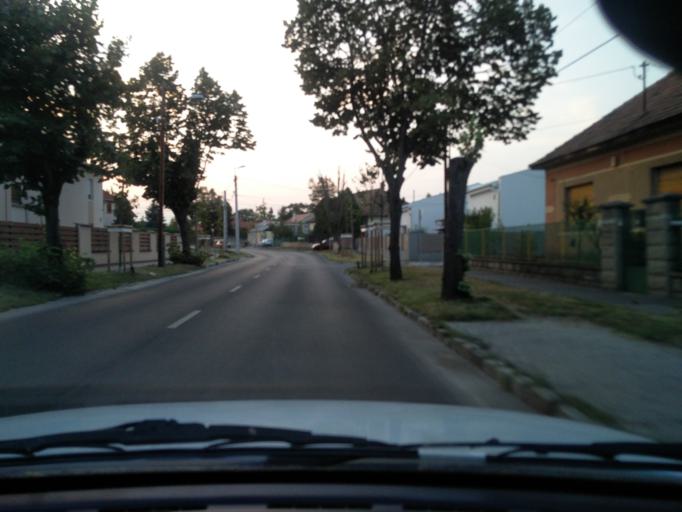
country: HU
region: Budapest
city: Budapest XXIII. keruelet
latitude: 47.3939
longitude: 19.1028
